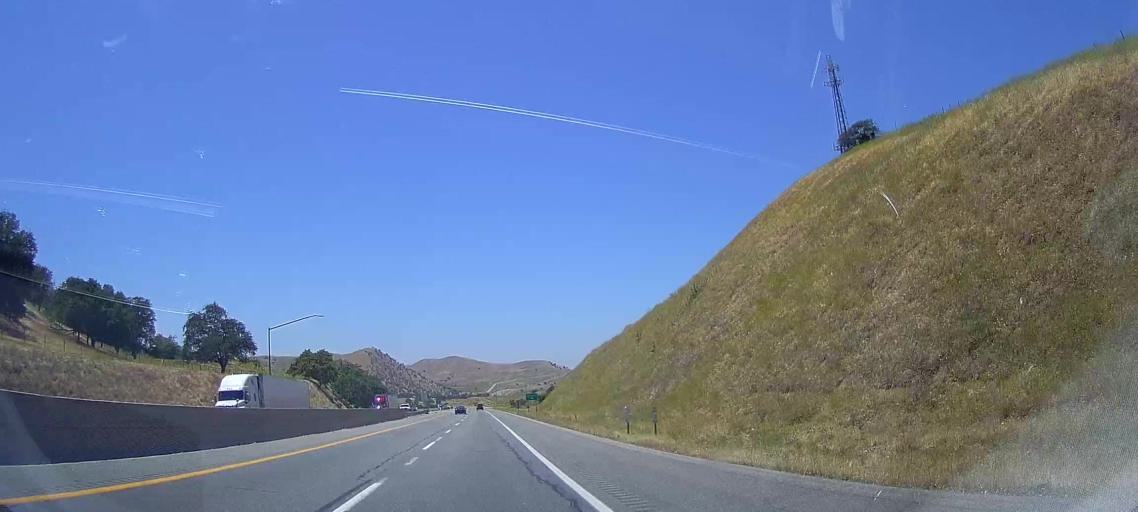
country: US
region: California
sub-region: Kern County
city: Bear Valley Springs
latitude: 35.2640
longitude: -118.6297
